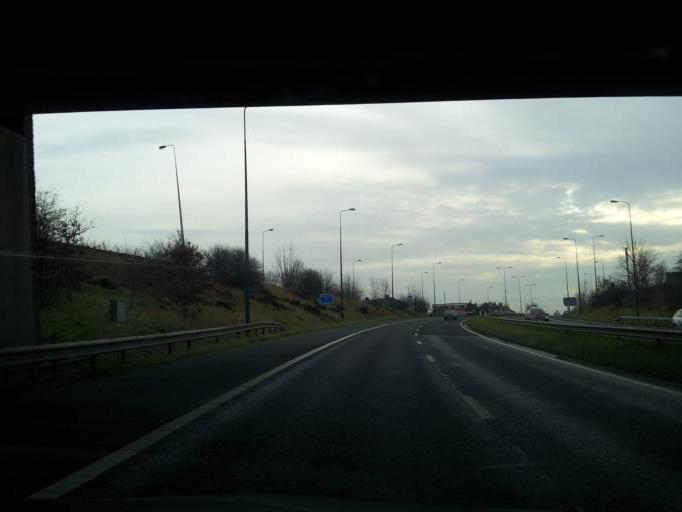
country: GB
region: England
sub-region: Borough of Oldham
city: Royton
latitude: 53.5561
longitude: -2.1398
